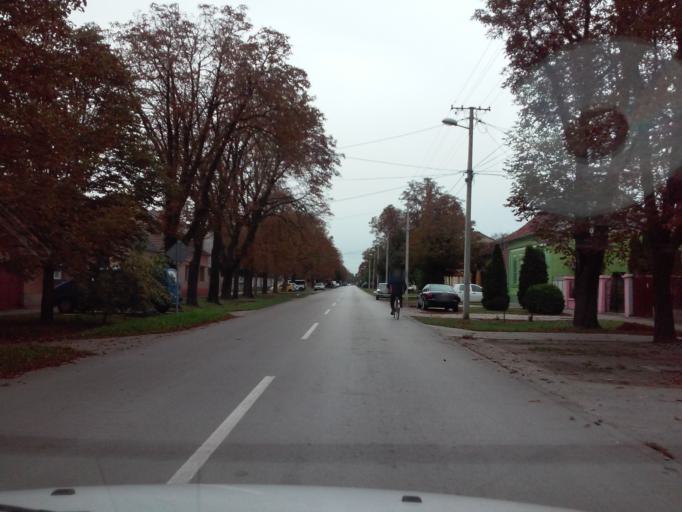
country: RS
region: Autonomna Pokrajina Vojvodina
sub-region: Severnobanatski Okrug
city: Kikinda
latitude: 45.8232
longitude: 20.4732
